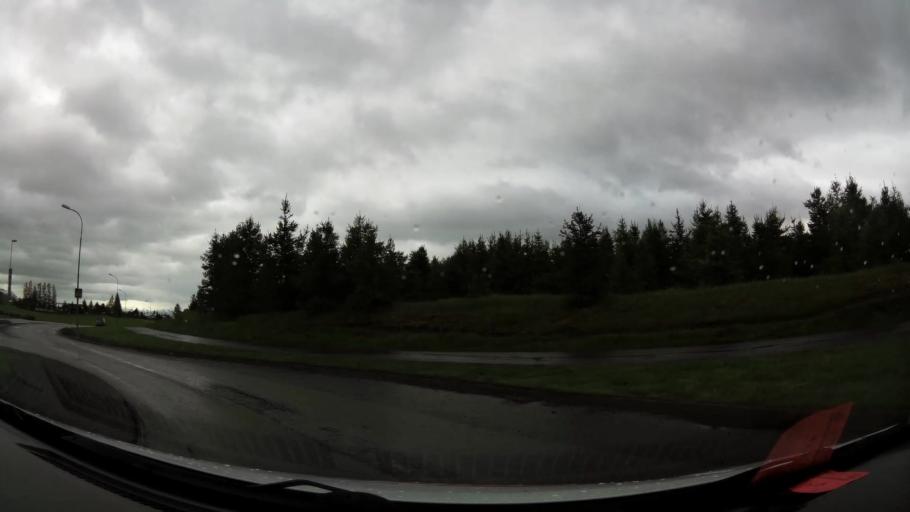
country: IS
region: Northeast
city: Akureyri
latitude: 65.6792
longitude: -18.1316
